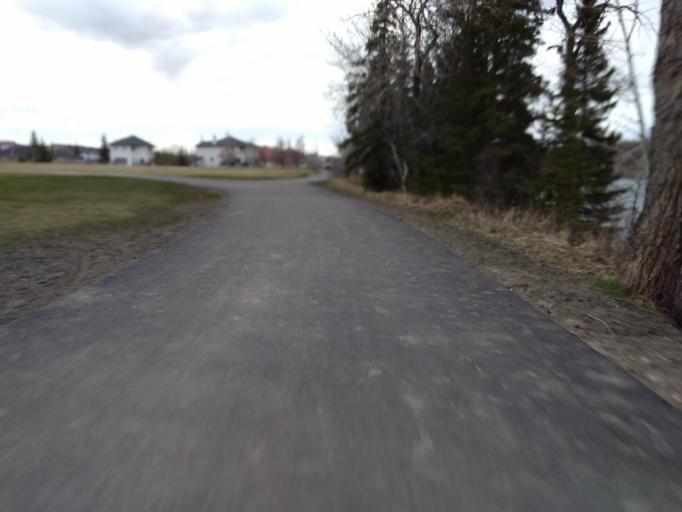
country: CA
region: Alberta
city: Cochrane
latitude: 51.1838
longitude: -114.4902
